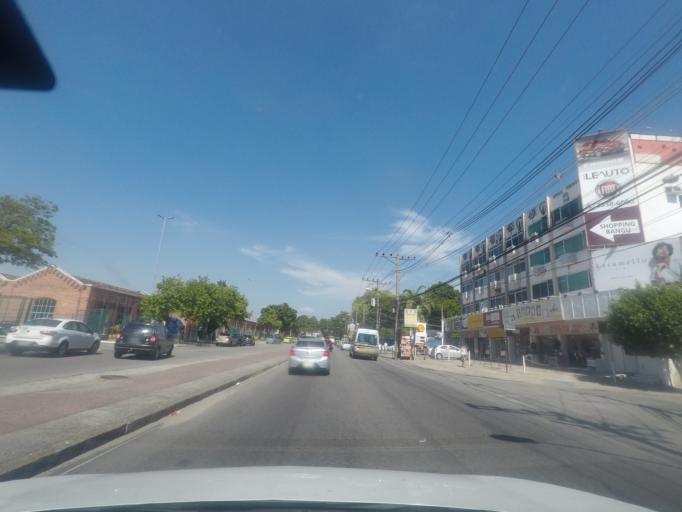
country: BR
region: Rio de Janeiro
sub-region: Nilopolis
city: Nilopolis
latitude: -22.8802
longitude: -43.4683
